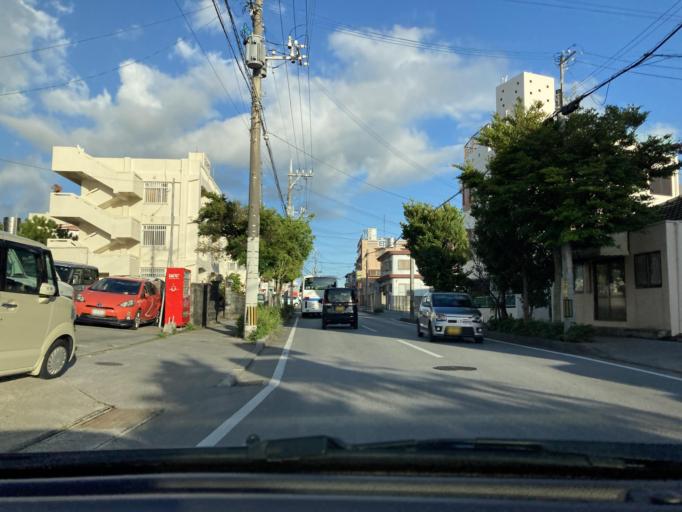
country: JP
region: Okinawa
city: Naha-shi
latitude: 26.2049
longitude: 127.7170
